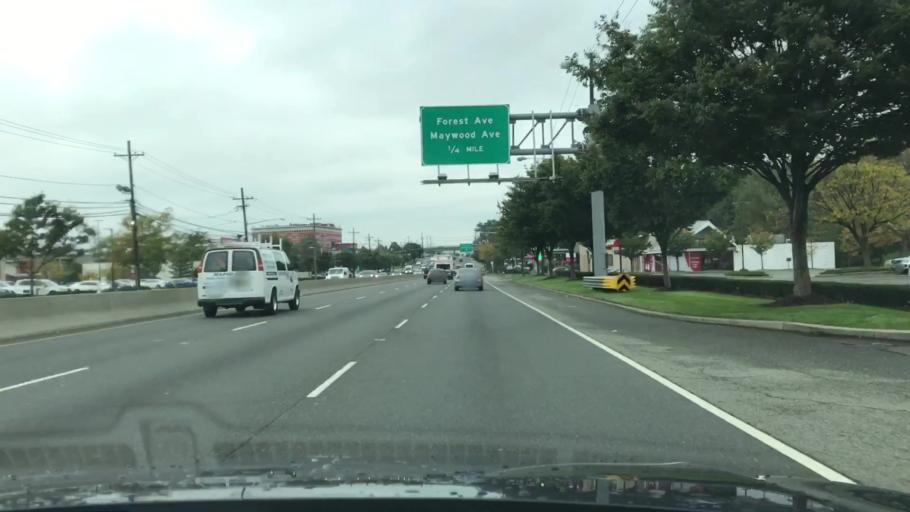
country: US
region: New Jersey
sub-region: Bergen County
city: River Edge
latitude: 40.9143
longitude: -74.0476
